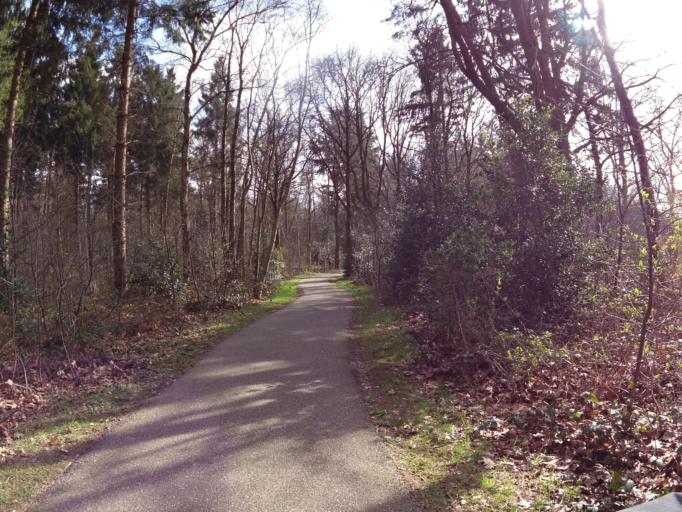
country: NL
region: Friesland
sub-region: Gemeente Weststellingwerf
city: Noordwolde
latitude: 52.8798
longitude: 6.2141
